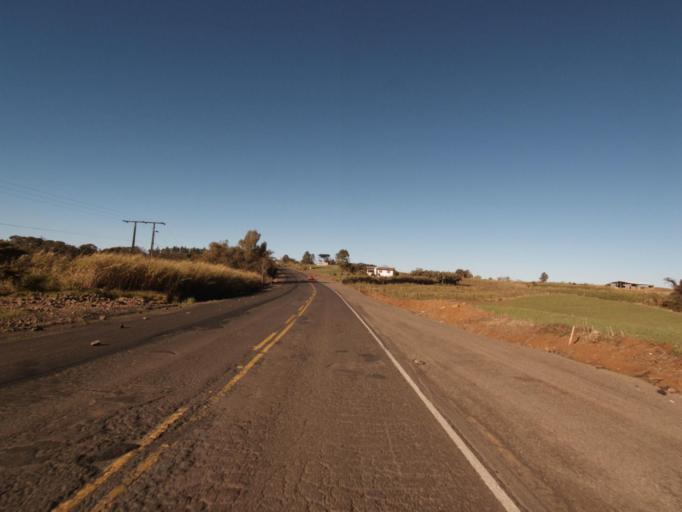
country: AR
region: Misiones
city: Bernardo de Irigoyen
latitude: -26.6456
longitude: -53.5192
